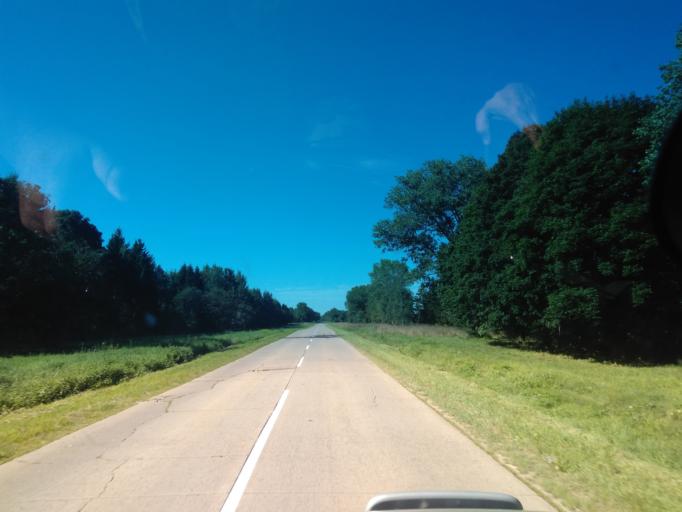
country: BY
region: Minsk
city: Stan'kava
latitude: 53.6514
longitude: 27.3087
